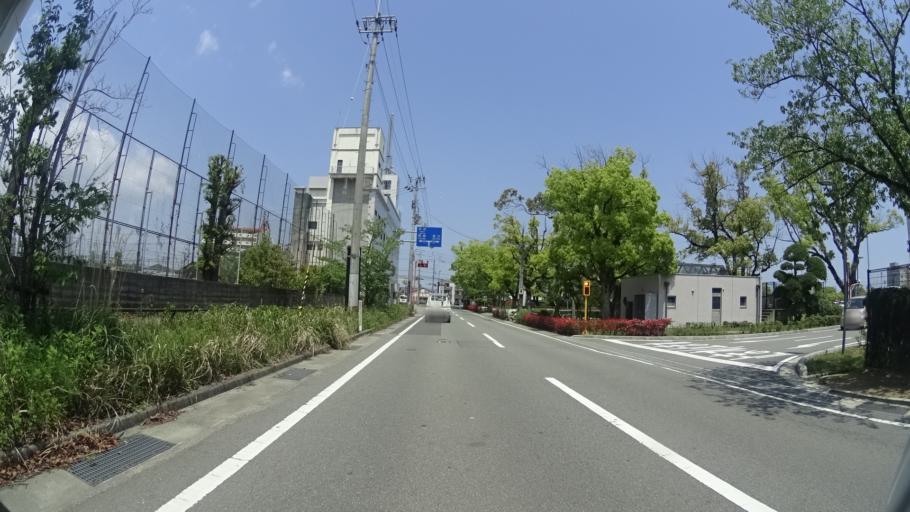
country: JP
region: Tokushima
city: Tokushima-shi
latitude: 34.0740
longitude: 134.5127
